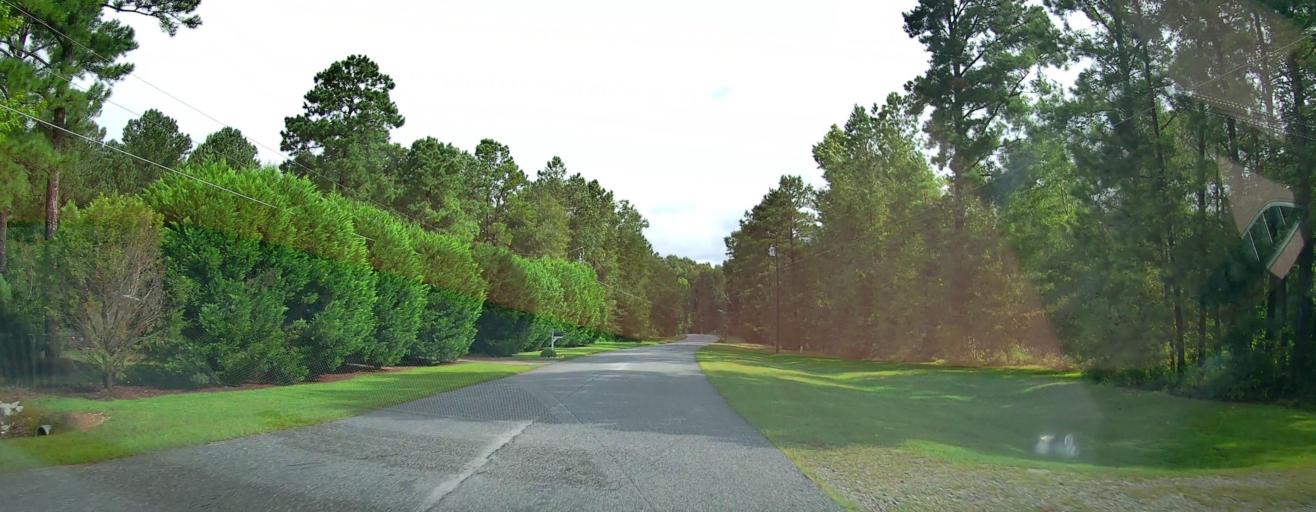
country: US
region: Georgia
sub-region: Bibb County
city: West Point
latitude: 32.7931
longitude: -83.7852
